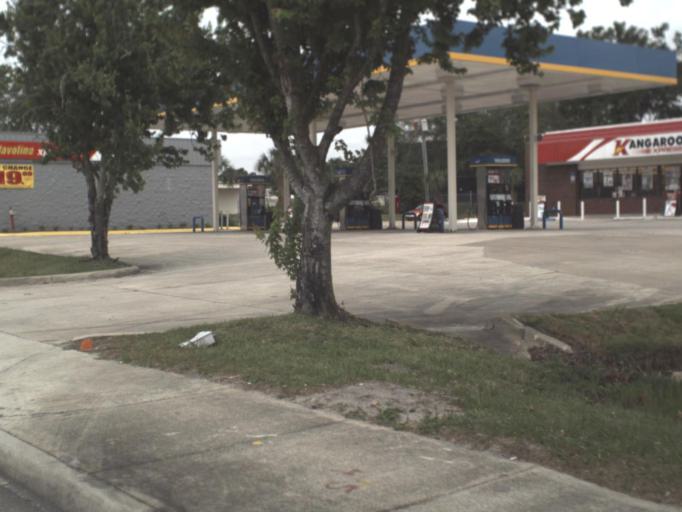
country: US
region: Florida
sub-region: Clay County
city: Lakeside
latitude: 30.1440
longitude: -81.7642
